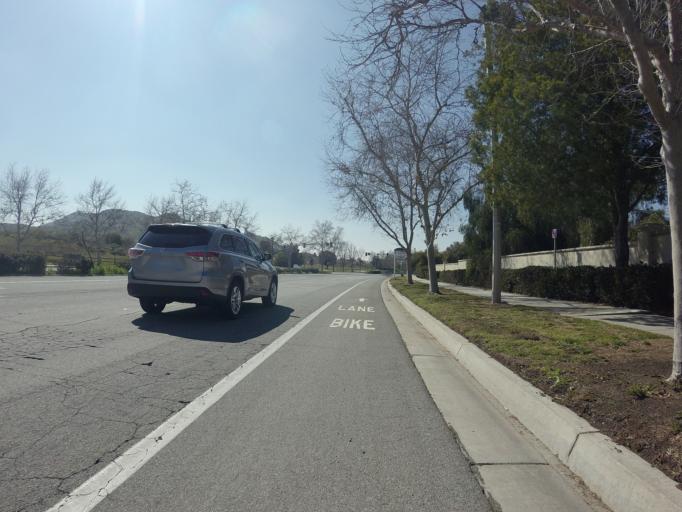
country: US
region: California
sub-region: Riverside County
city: Moreno Valley
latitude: 33.8957
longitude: -117.1779
